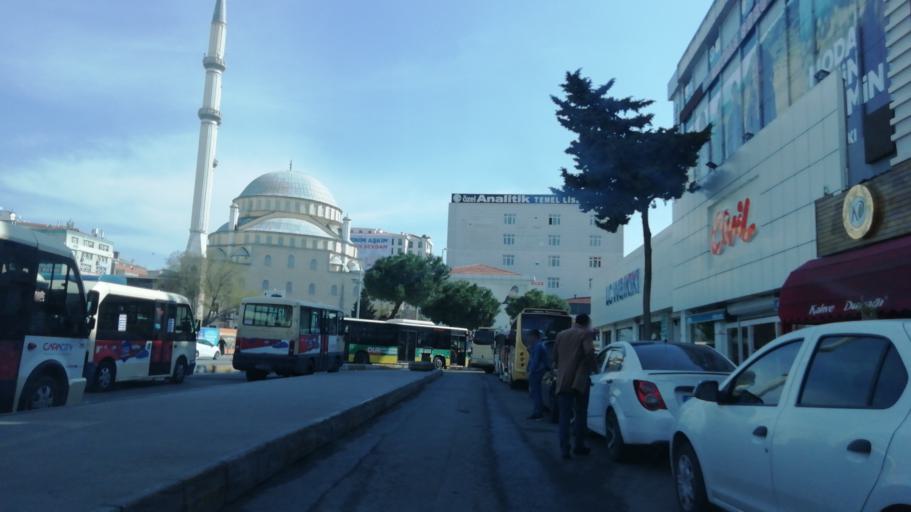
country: TR
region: Istanbul
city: Bagcilar
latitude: 41.0337
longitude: 28.8558
